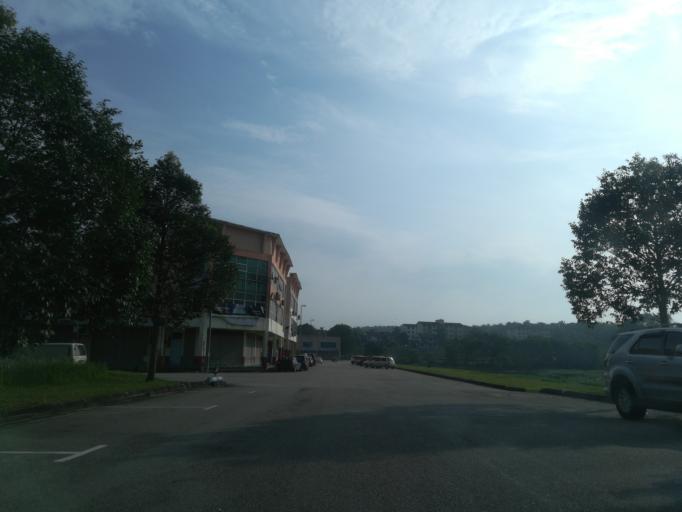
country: MY
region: Kedah
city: Kulim
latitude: 5.3874
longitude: 100.5720
